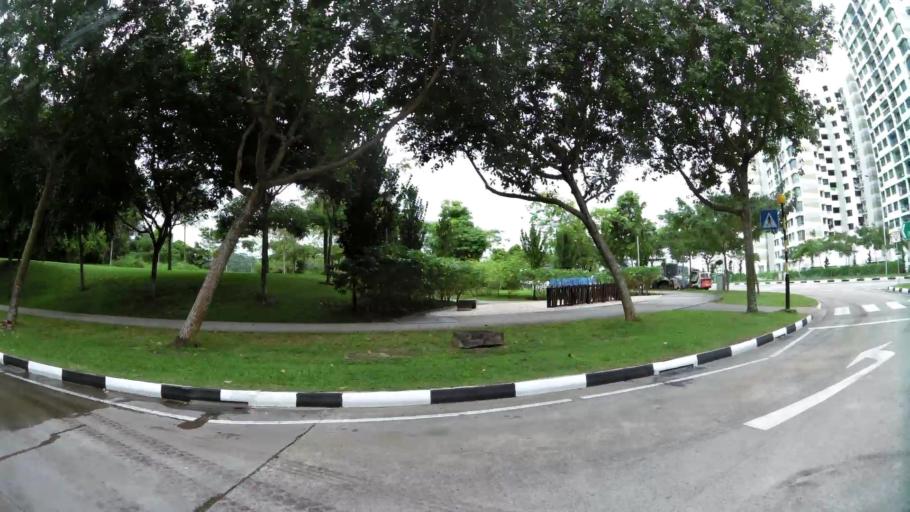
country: MY
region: Johor
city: Kampung Pasir Gudang Baru
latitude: 1.4062
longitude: 103.9075
